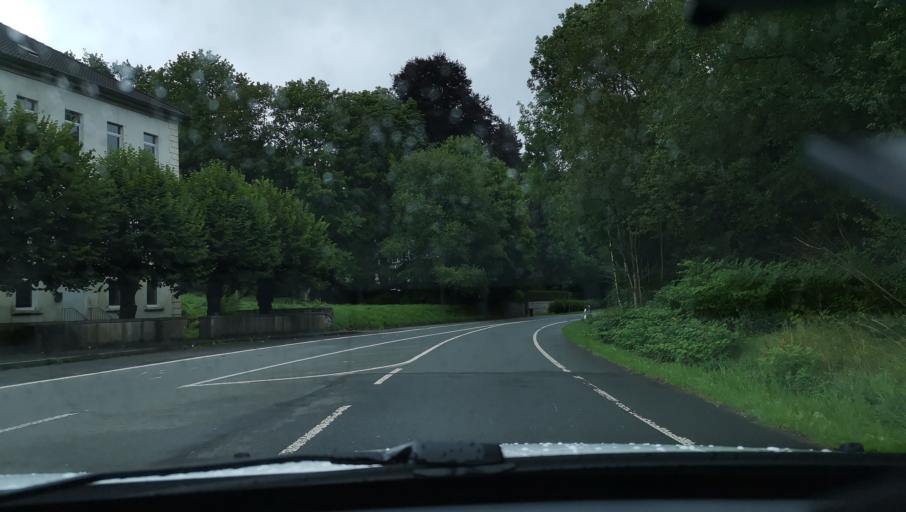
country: DE
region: North Rhine-Westphalia
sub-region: Regierungsbezirk Arnsberg
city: Schalksmuhle
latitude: 51.2139
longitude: 7.5270
